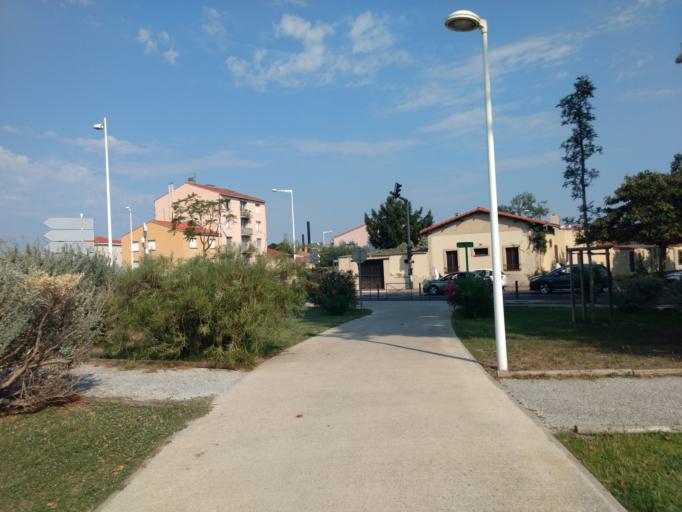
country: FR
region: Languedoc-Roussillon
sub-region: Departement des Pyrenees-Orientales
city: Perpignan
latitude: 42.7068
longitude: 2.9009
